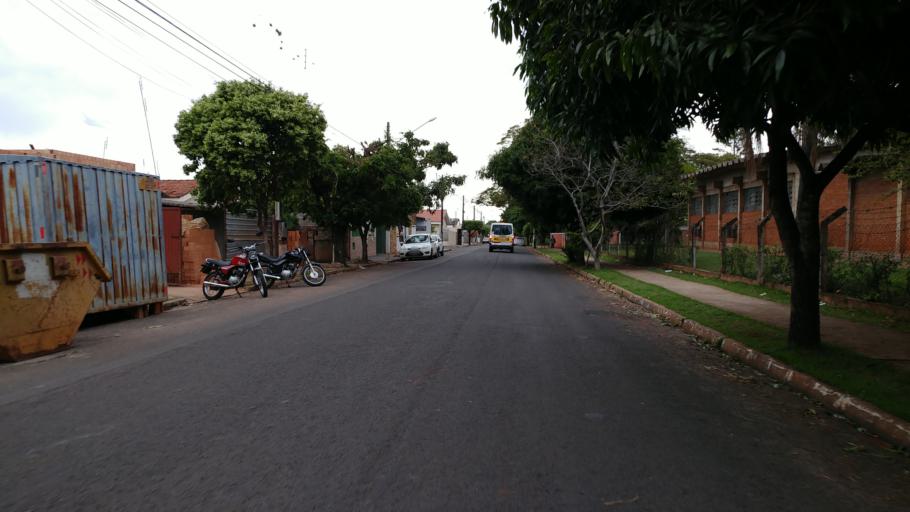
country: BR
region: Sao Paulo
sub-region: Paraguacu Paulista
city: Paraguacu Paulista
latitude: -22.4169
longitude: -50.5816
